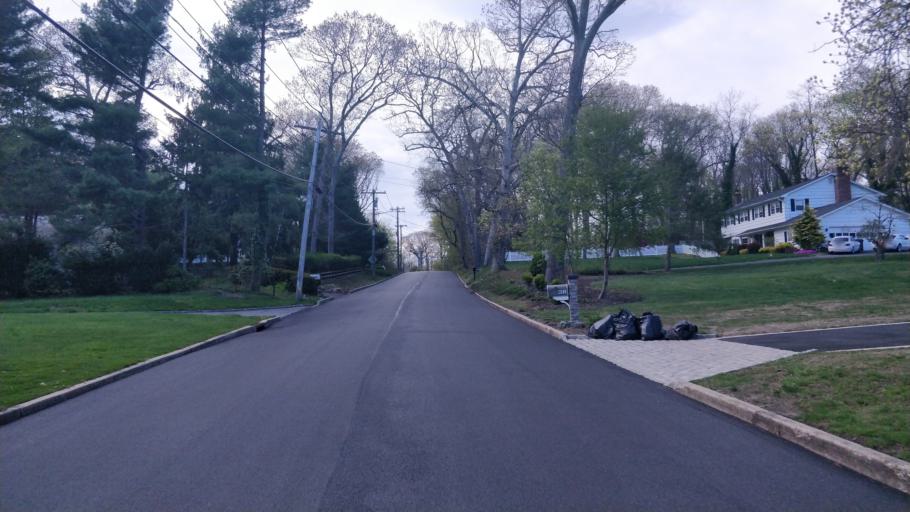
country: US
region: New York
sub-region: Suffolk County
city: Smithtown
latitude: 40.8787
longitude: -73.2089
